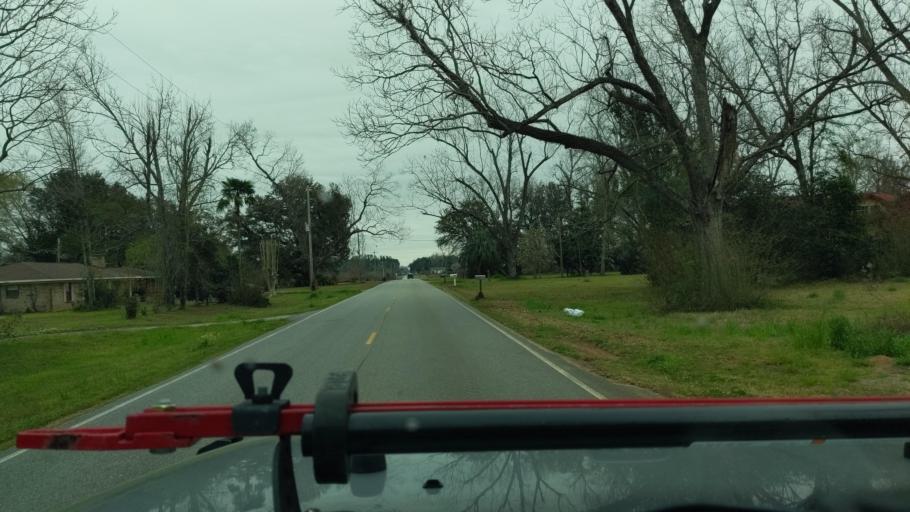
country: US
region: Alabama
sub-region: Baldwin County
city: Foley
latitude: 30.4579
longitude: -87.7499
